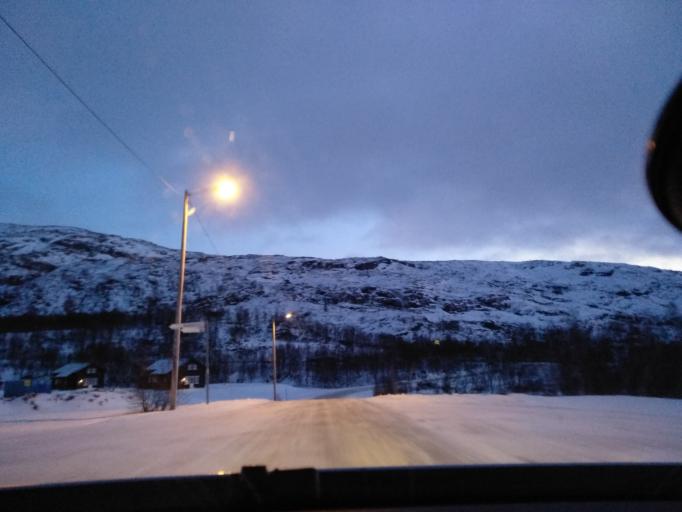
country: NO
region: Vest-Agder
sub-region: Sirdal
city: Tonstad
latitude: 59.0142
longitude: 6.9385
